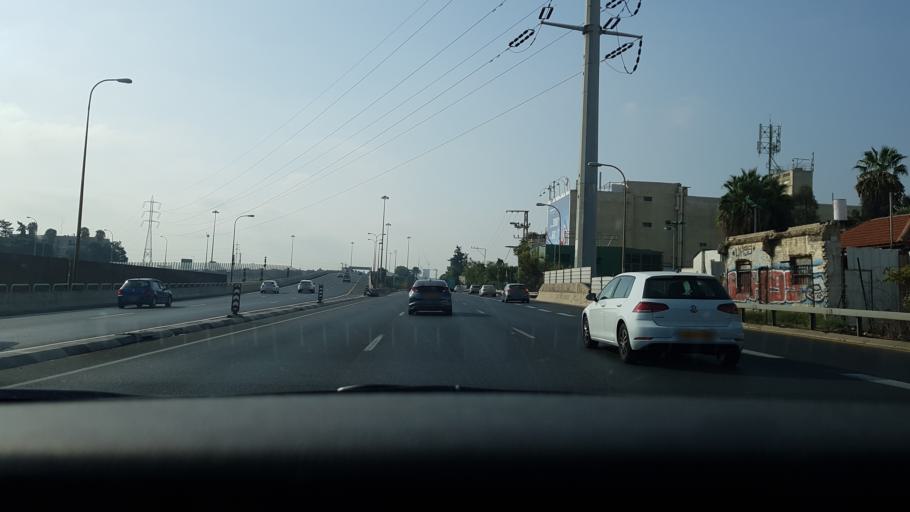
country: IL
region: Tel Aviv
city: Tel Aviv
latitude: 32.0538
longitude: 34.7842
